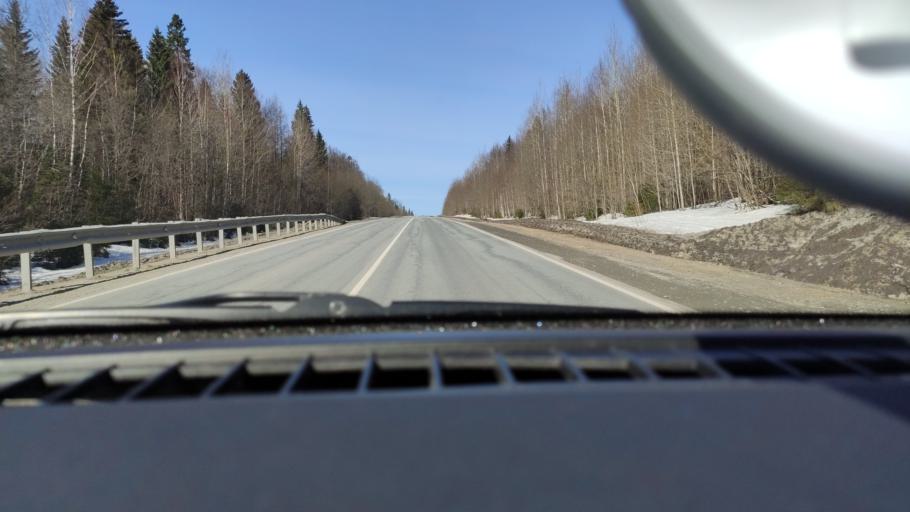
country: RU
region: Perm
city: Perm
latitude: 58.1660
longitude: 56.2399
